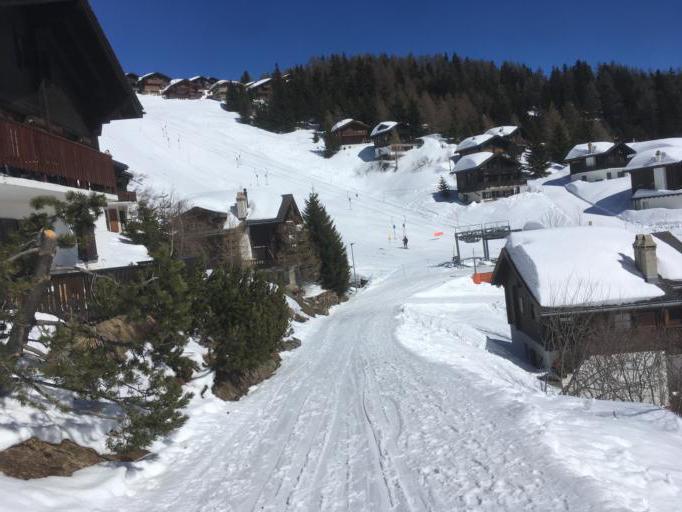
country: CH
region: Valais
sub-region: Goms District
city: Fiesch
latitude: 46.3891
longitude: 8.0637
